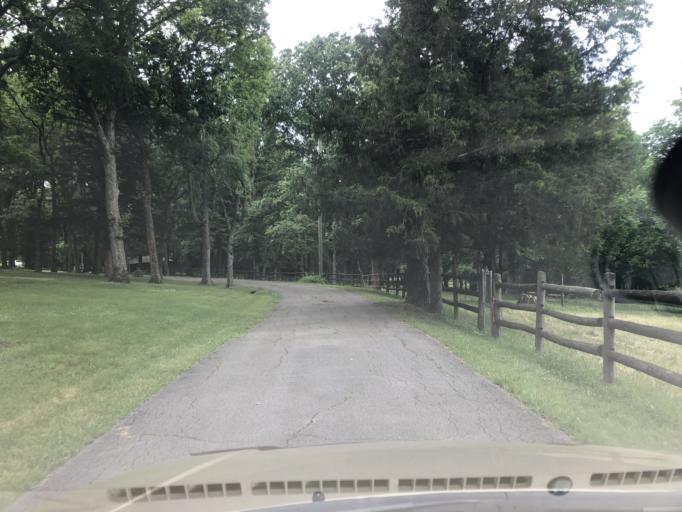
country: US
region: Tennessee
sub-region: Davidson County
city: Lakewood
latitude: 36.2236
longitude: -86.6465
